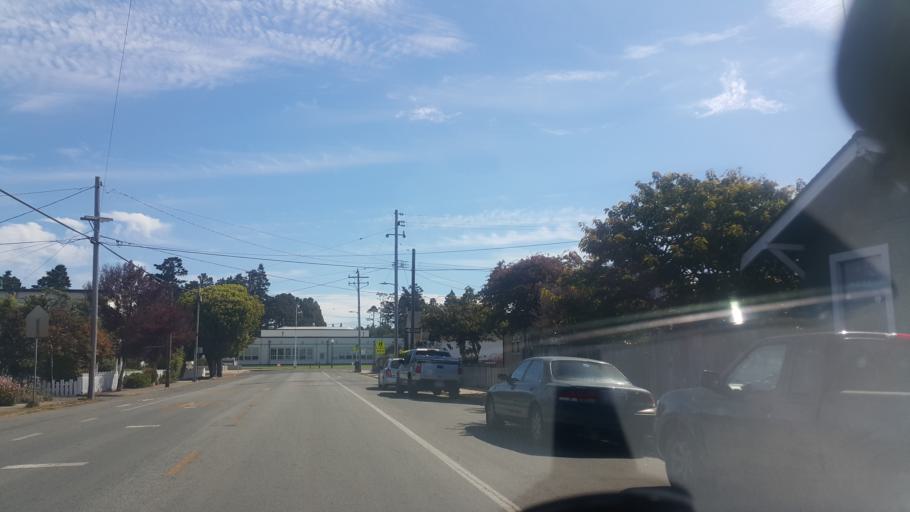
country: US
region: California
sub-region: Mendocino County
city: Fort Bragg
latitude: 39.4479
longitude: -123.7995
